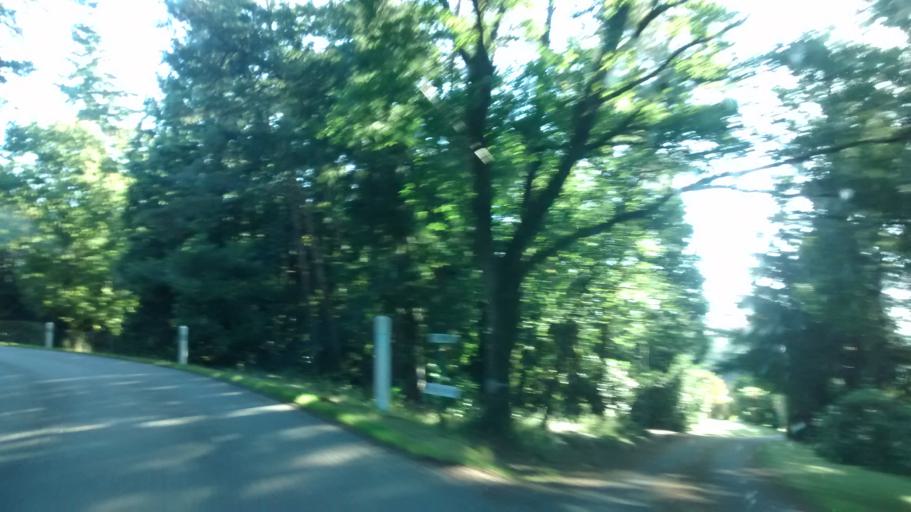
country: FR
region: Brittany
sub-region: Departement du Morbihan
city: Campeneac
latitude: 47.9844
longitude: -2.3060
